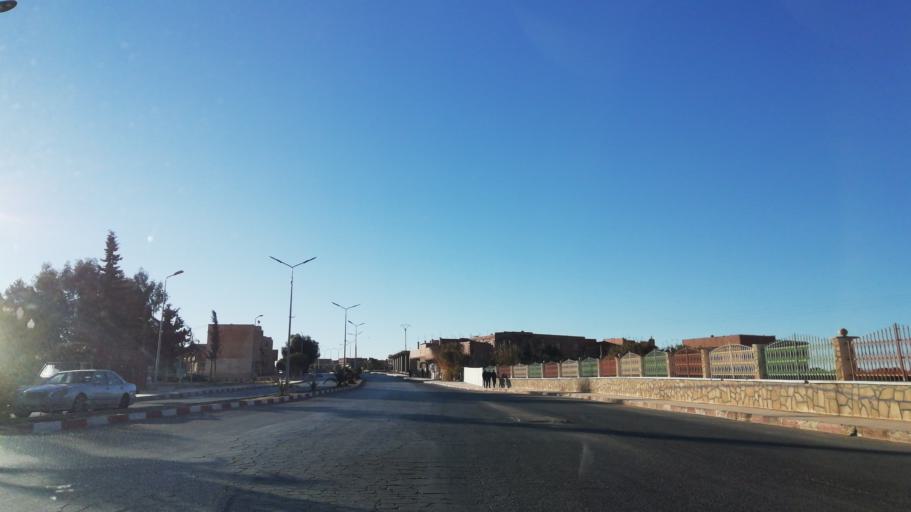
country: DZ
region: Saida
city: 'Ain el Hadjar
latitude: 34.0352
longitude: 0.0875
